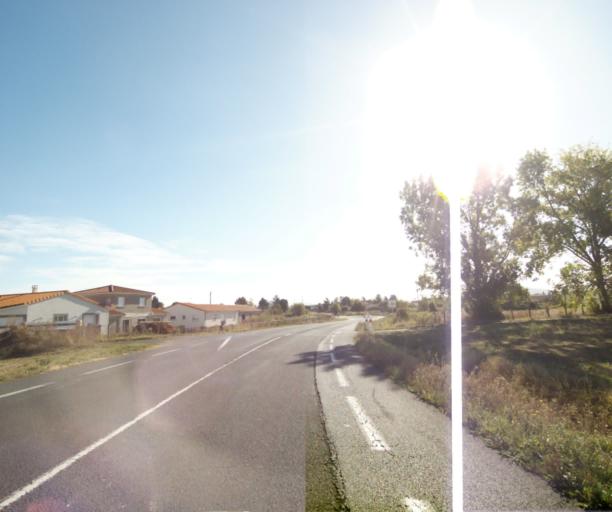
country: FR
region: Auvergne
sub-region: Departement du Puy-de-Dome
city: Malintrat
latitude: 45.8110
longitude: 3.1873
